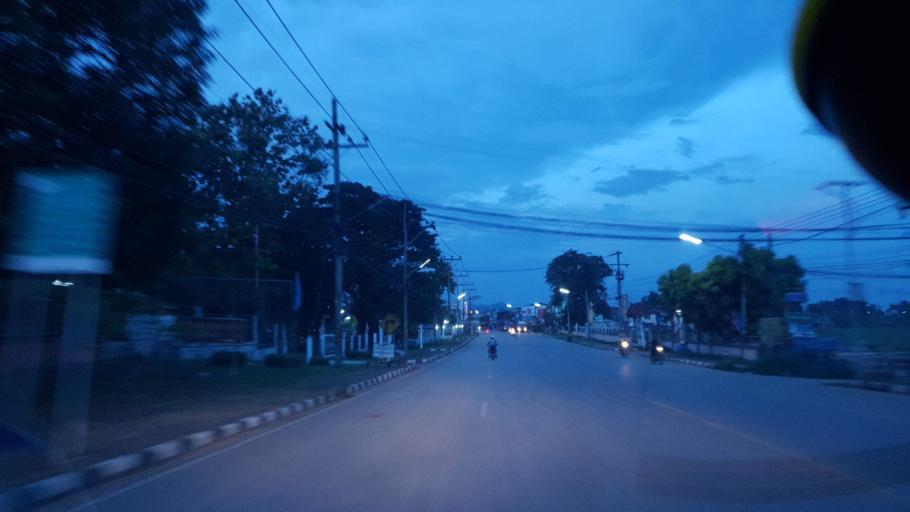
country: TH
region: Chiang Rai
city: Wiang Chiang Rung
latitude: 20.0024
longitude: 100.0408
